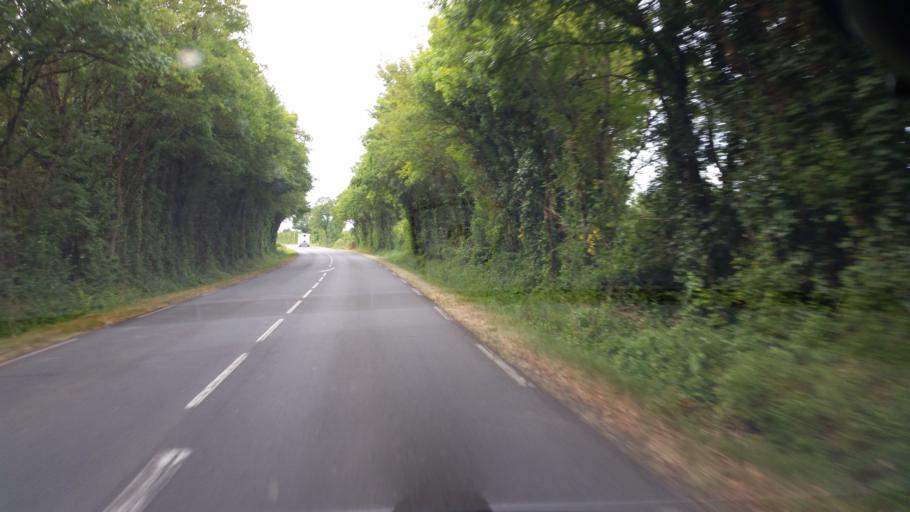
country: FR
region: Poitou-Charentes
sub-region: Departement de la Charente-Maritime
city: Surgeres
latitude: 46.1221
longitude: -0.7675
